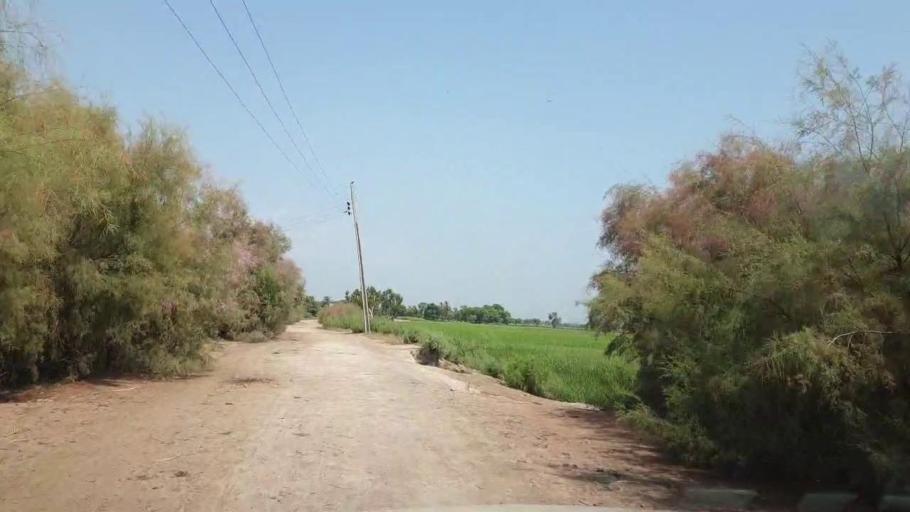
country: PK
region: Sindh
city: Ratodero
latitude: 27.8422
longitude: 68.2469
